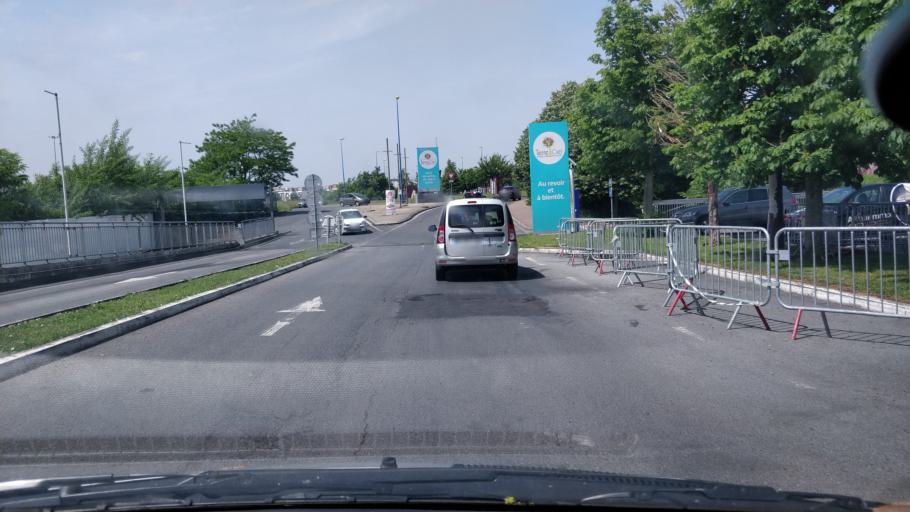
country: FR
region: Ile-de-France
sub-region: Departement de Seine-et-Marne
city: Chelles
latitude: 48.8771
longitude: 2.6099
